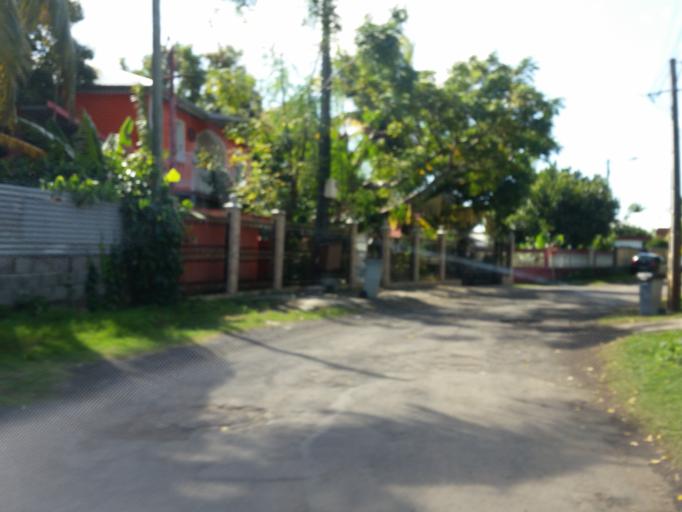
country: RE
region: Reunion
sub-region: Reunion
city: Sainte-Marie
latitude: -20.8956
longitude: 55.5307
